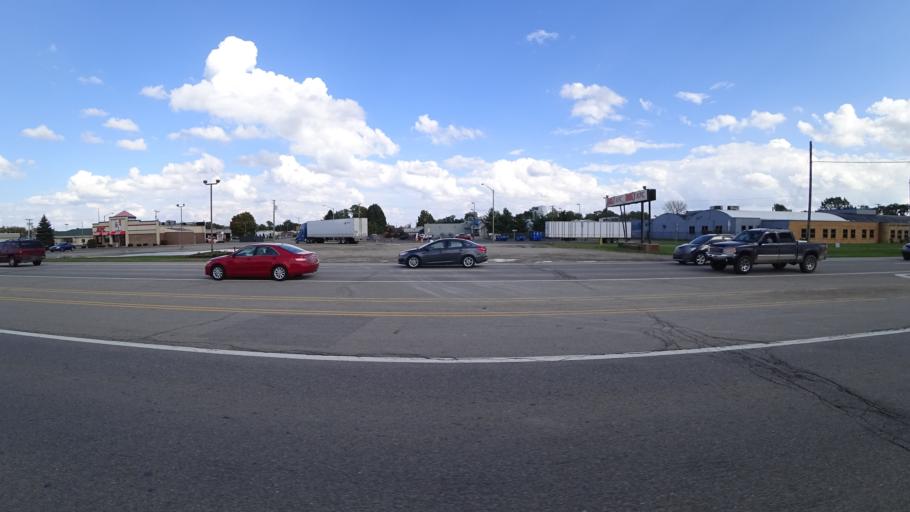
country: US
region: Michigan
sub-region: Saint Joseph County
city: Three Rivers
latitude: 41.9417
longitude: -85.6517
